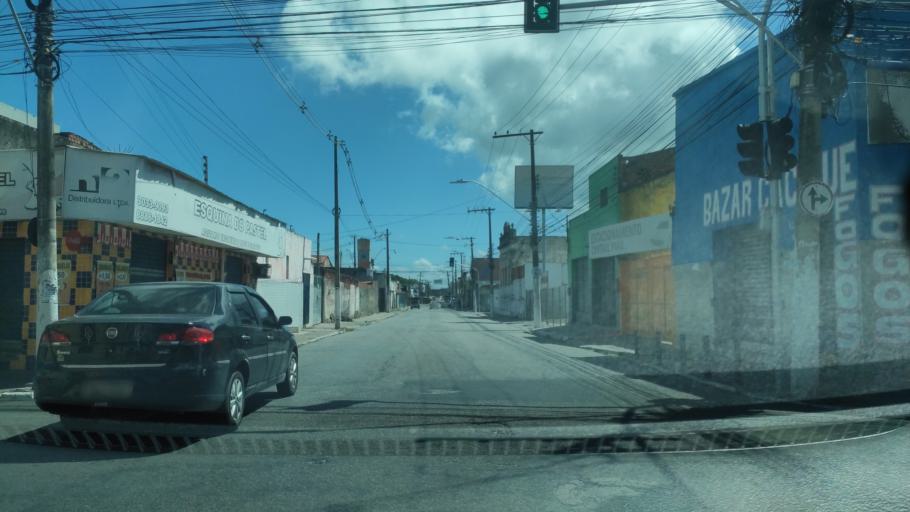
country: BR
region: Alagoas
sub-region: Maceio
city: Maceio
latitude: -9.6613
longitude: -35.7418
